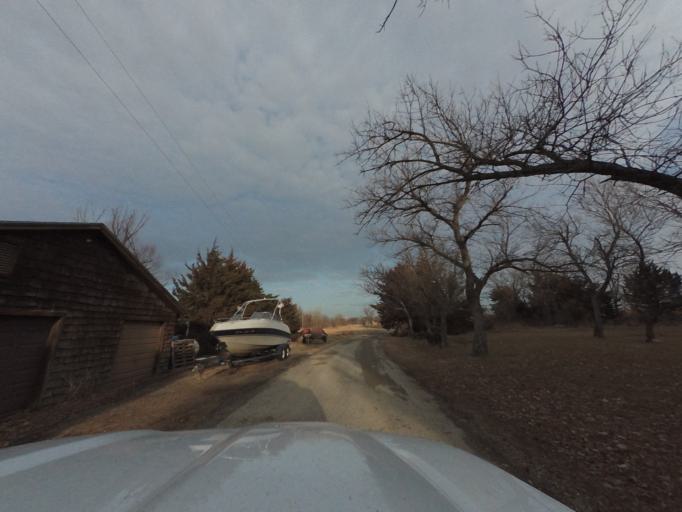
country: US
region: Kansas
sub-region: Morris County
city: Council Grove
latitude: 38.5242
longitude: -96.4253
